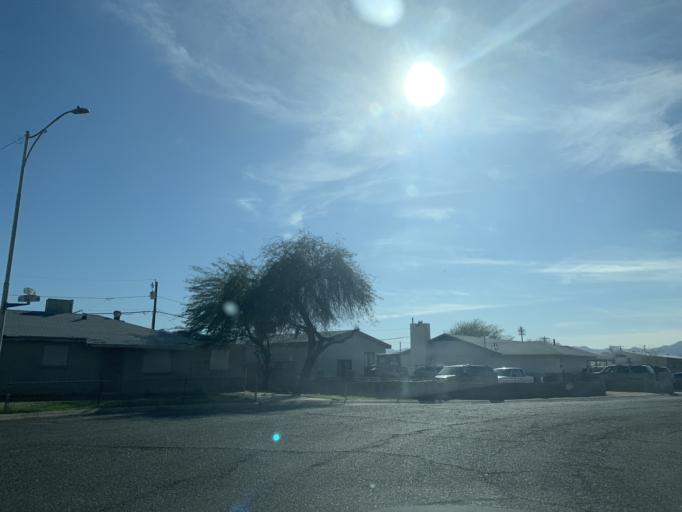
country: US
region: Arizona
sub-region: Maricopa County
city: Laveen
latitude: 33.3963
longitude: -112.1347
